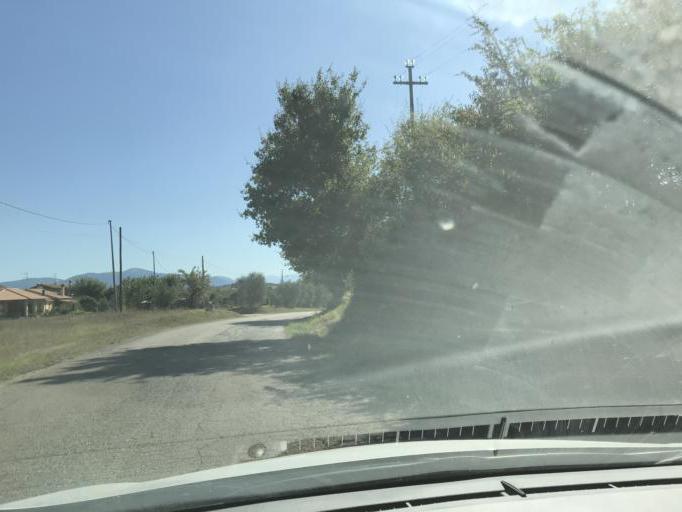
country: IT
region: Umbria
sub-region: Provincia di Terni
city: Avigliano Umbro
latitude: 42.6187
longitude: 12.4191
